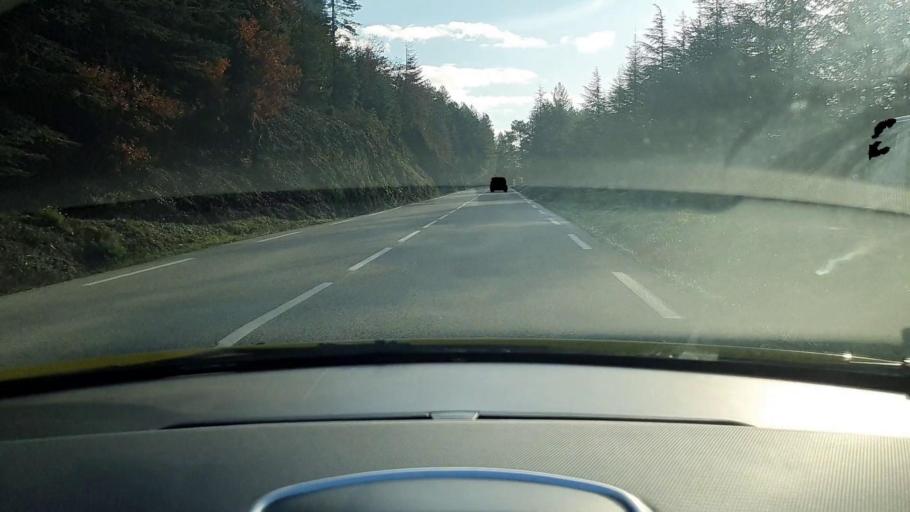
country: FR
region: Languedoc-Roussillon
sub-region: Departement du Gard
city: Branoux-les-Taillades
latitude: 44.3660
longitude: 3.9418
